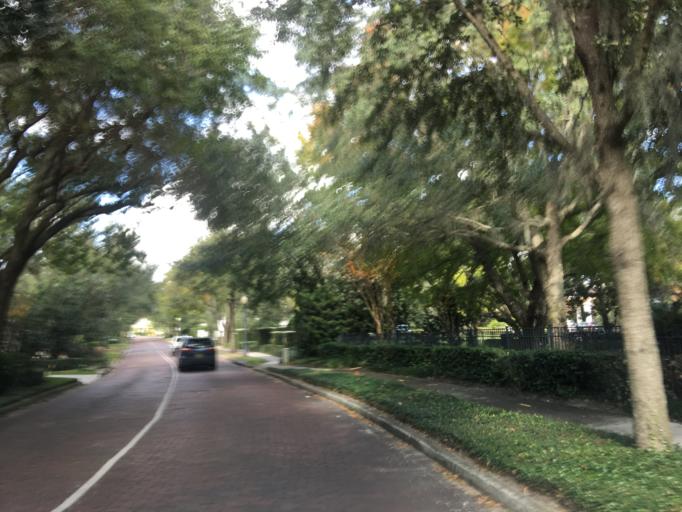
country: US
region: Florida
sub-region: Orange County
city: Winter Park
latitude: 28.6086
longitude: -81.3511
